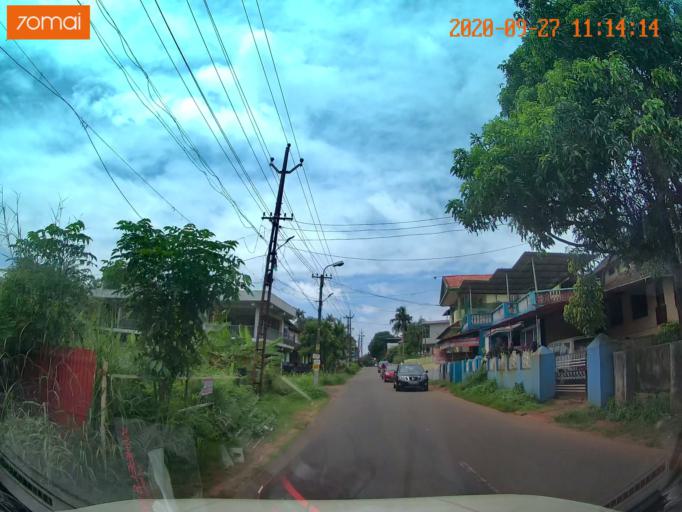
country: IN
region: Kerala
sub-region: Thrissur District
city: Thanniyam
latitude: 10.4334
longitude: 76.2070
